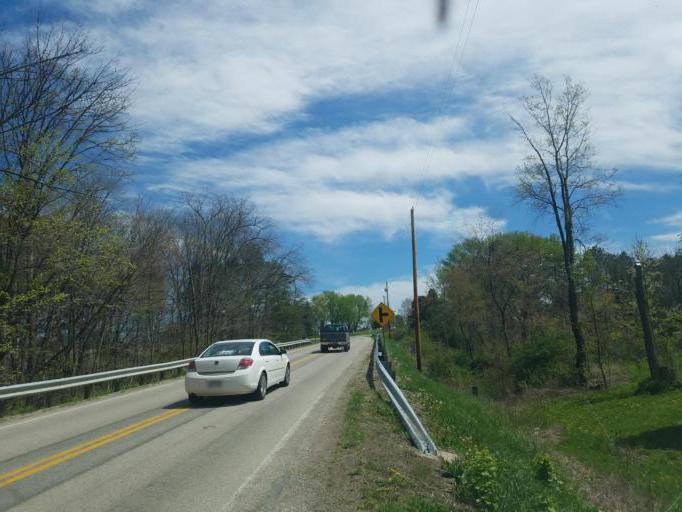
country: US
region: Ohio
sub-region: Ashland County
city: Ashland
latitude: 40.7738
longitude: -82.3561
